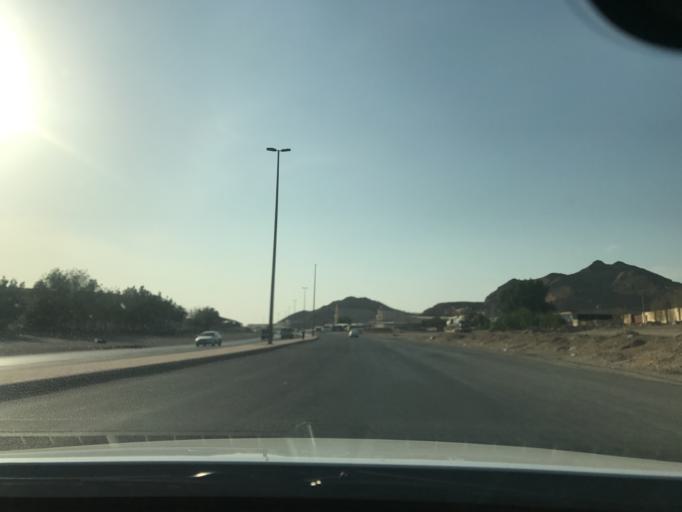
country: SA
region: Makkah
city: Jeddah
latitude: 21.4080
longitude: 39.4264
